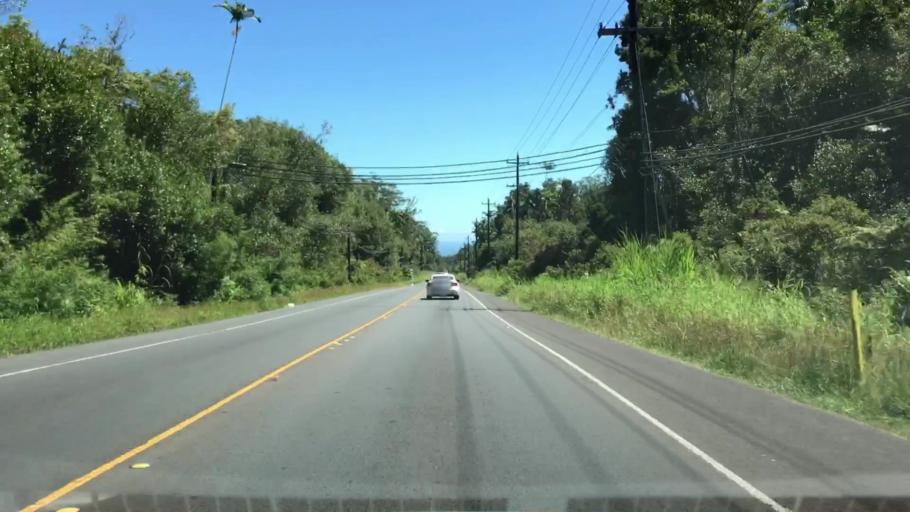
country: US
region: Hawaii
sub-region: Hawaii County
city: Mountain View
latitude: 19.5309
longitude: -155.1312
